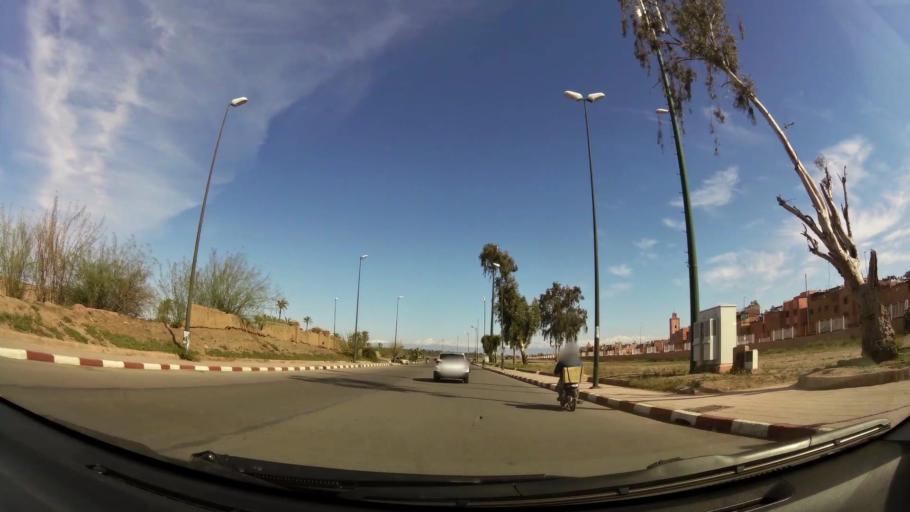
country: MA
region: Marrakech-Tensift-Al Haouz
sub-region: Marrakech
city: Marrakesh
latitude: 31.6219
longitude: -7.9682
